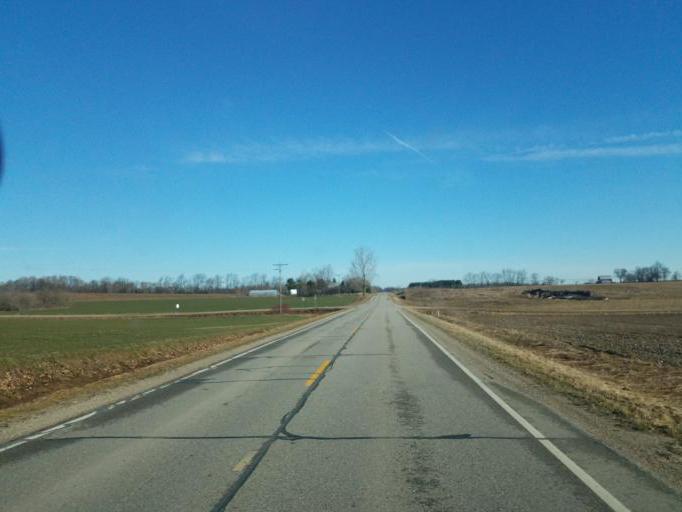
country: US
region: Michigan
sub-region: Montcalm County
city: Edmore
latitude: 43.4867
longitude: -85.0851
